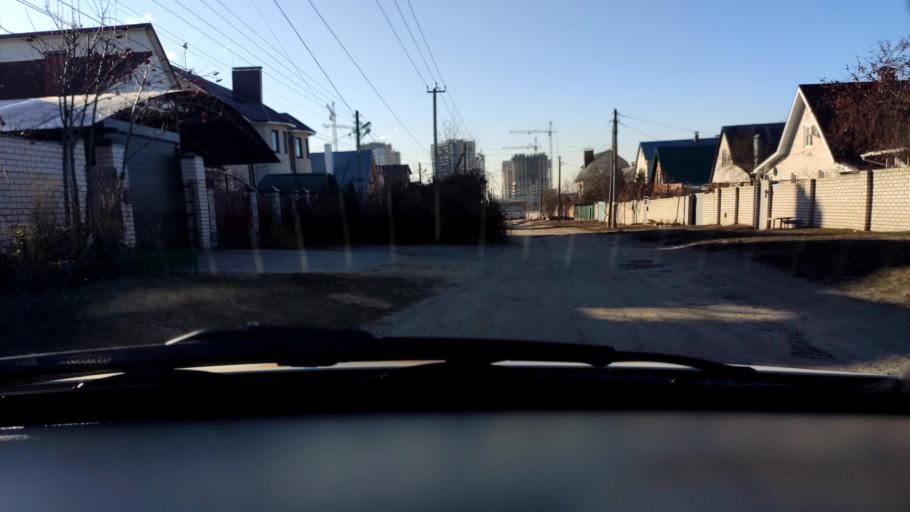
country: RU
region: Voronezj
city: Podgornoye
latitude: 51.7231
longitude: 39.1507
